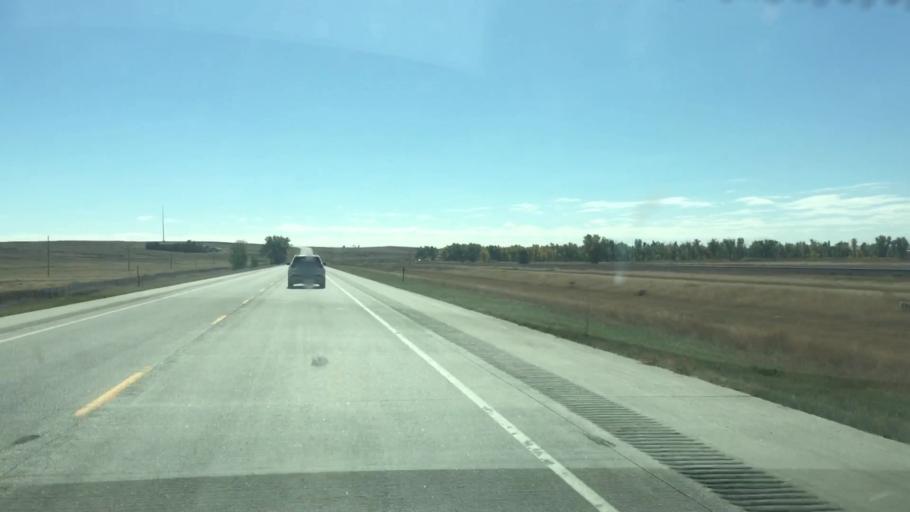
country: US
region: Colorado
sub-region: Lincoln County
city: Limon
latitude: 39.2235
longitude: -103.6097
